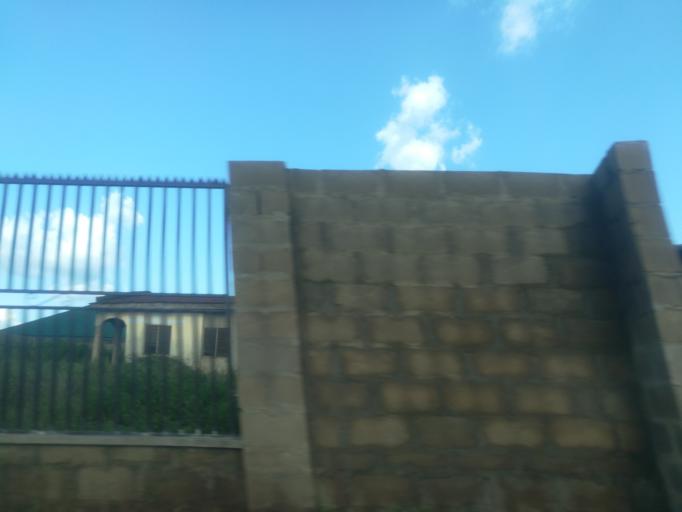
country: NG
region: Oyo
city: Lalupon
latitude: 7.4373
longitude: 3.9822
